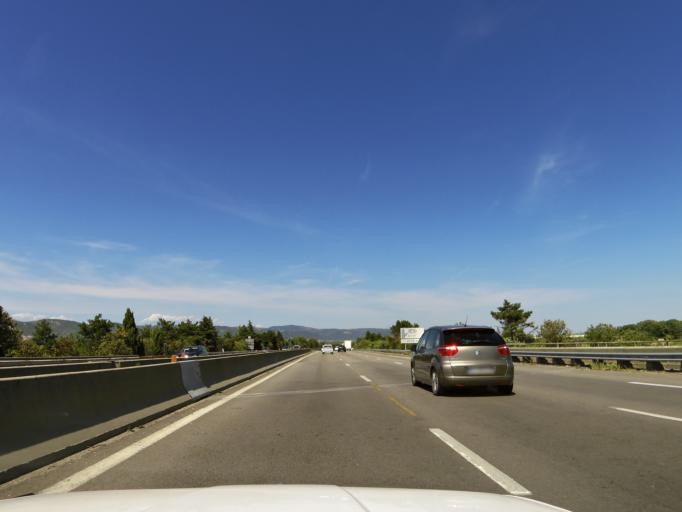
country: FR
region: Rhone-Alpes
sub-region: Departement de la Drome
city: Loriol-sur-Drome
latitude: 44.7399
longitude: 4.7895
